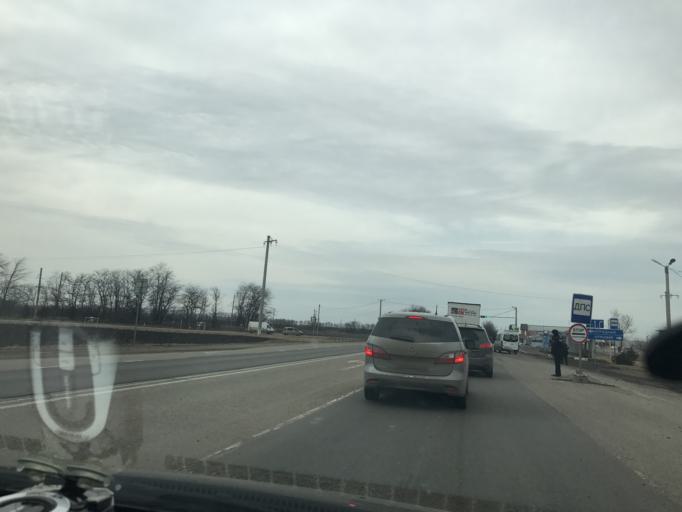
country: RU
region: Krasnodarskiy
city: Zavetnyy
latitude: 44.9232
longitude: 41.1322
